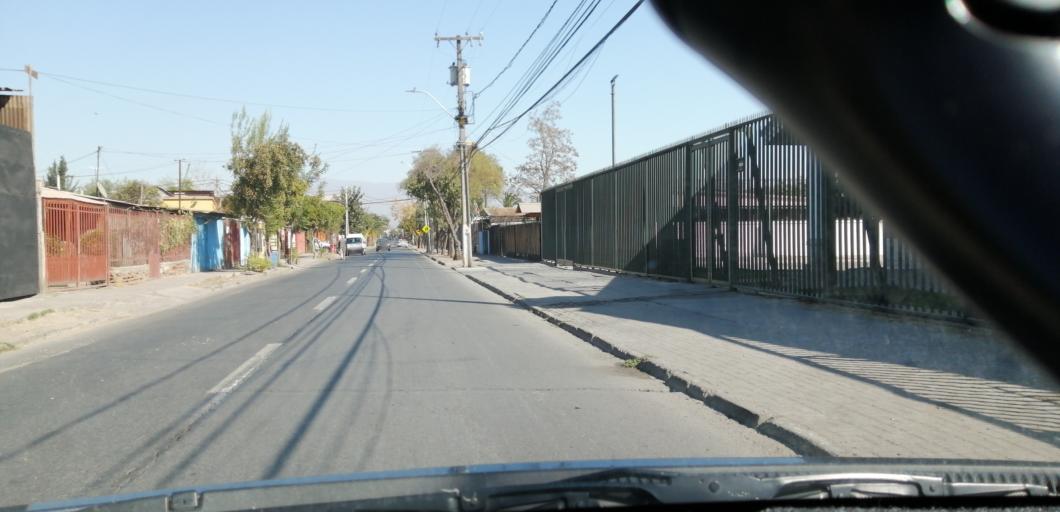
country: CL
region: Santiago Metropolitan
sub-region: Provincia de Santiago
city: Lo Prado
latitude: -33.4422
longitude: -70.7502
